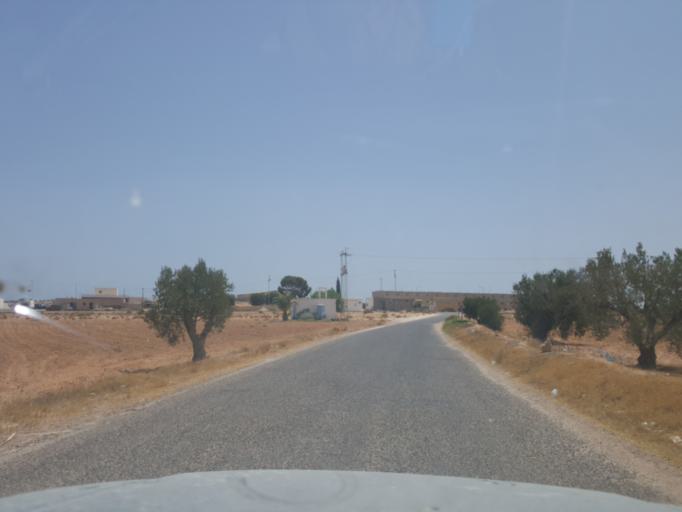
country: TN
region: Qabis
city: Gabes
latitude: 34.0548
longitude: 9.9835
